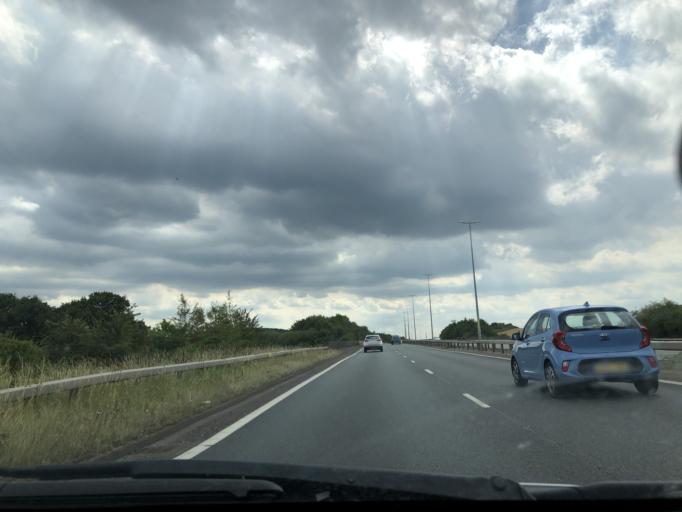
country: GB
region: England
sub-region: Kent
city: Tankerton
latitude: 51.3422
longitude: 1.0628
